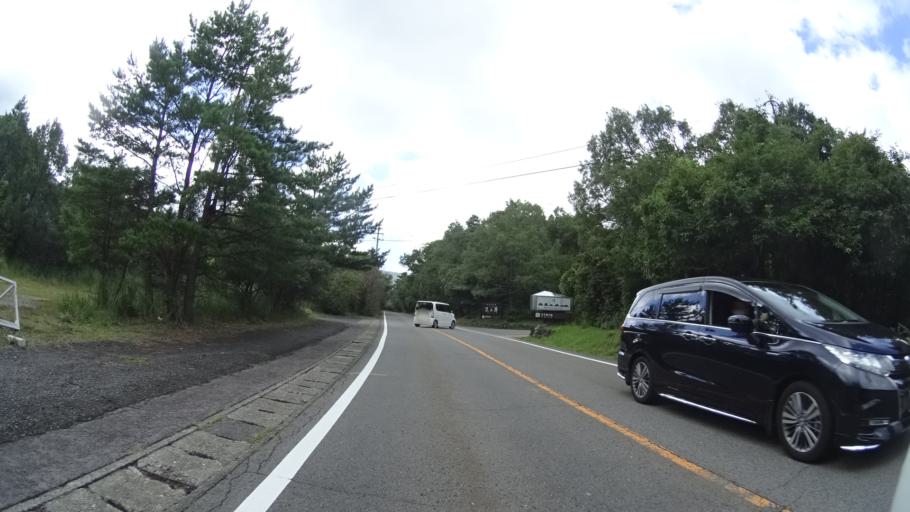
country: JP
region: Oita
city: Tsukawaki
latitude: 33.1174
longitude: 131.2284
